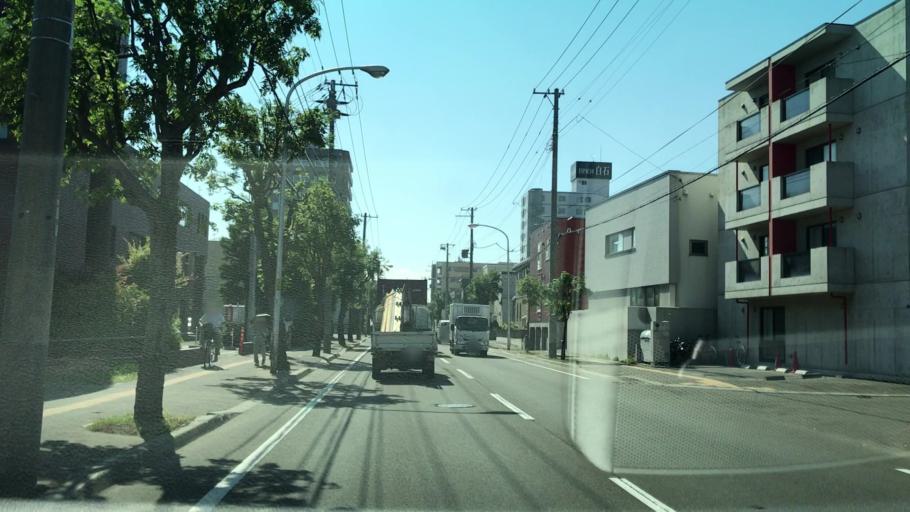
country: JP
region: Hokkaido
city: Sapporo
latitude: 43.0539
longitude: 141.4085
